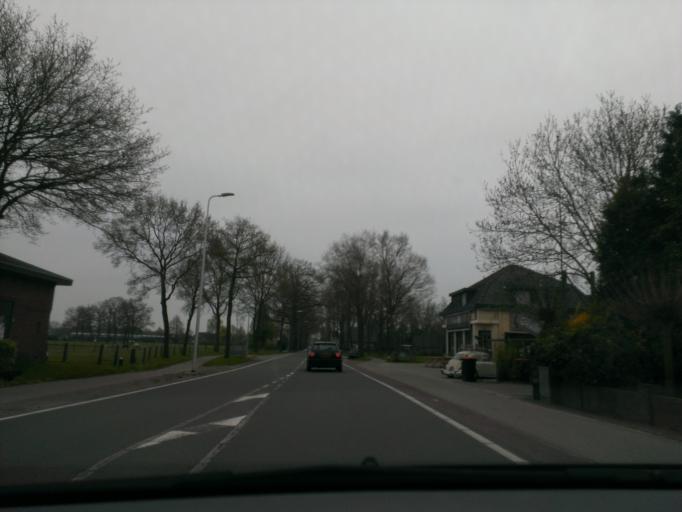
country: NL
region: Gelderland
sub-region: Gemeente Epe
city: Epe
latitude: 52.3354
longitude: 5.9806
